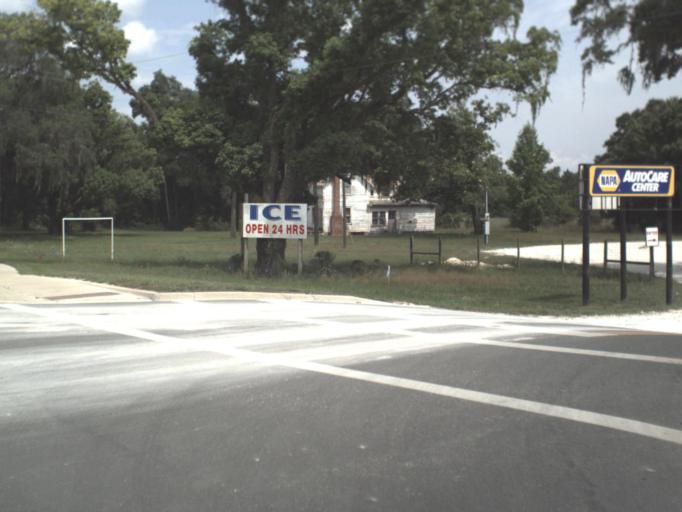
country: US
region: Florida
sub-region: Putnam County
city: Interlachen
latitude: 29.6289
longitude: -81.8807
